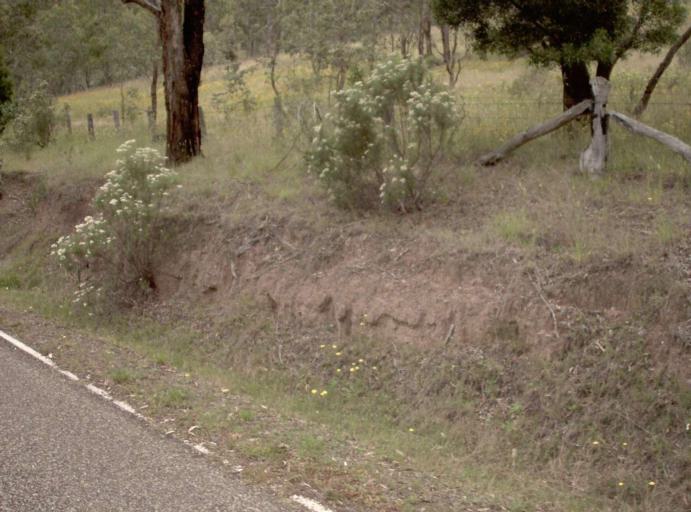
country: AU
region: Victoria
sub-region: East Gippsland
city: Bairnsdale
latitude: -37.5300
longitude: 147.2225
